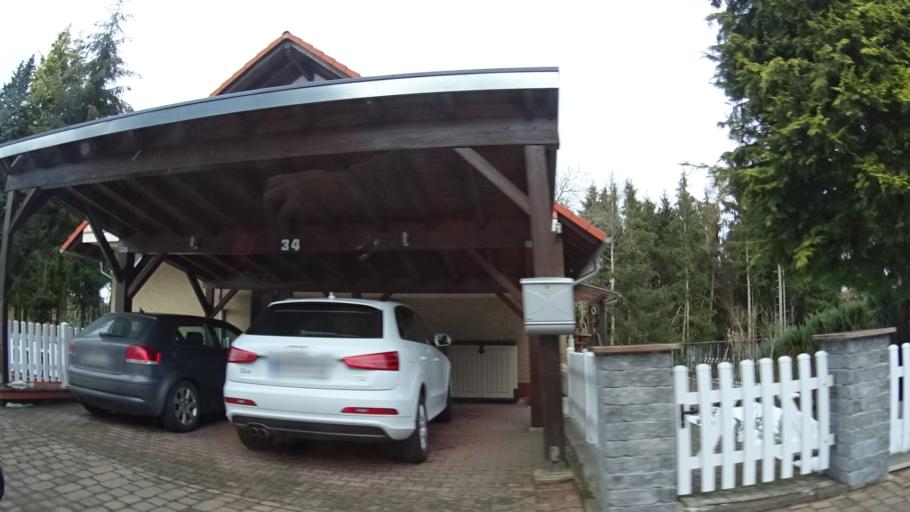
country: DE
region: Hesse
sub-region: Regierungsbezirk Darmstadt
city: Hesseneck
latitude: 49.6450
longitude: 9.0862
